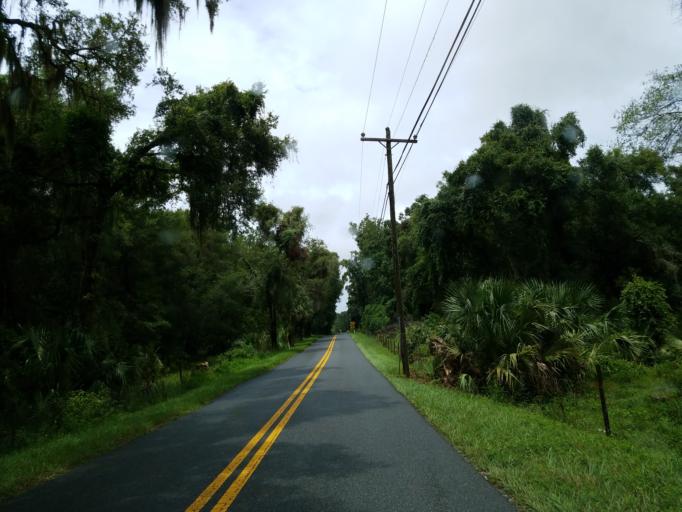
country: US
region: Florida
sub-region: Citrus County
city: Inverness Highlands South
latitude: 28.8074
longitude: -82.2954
